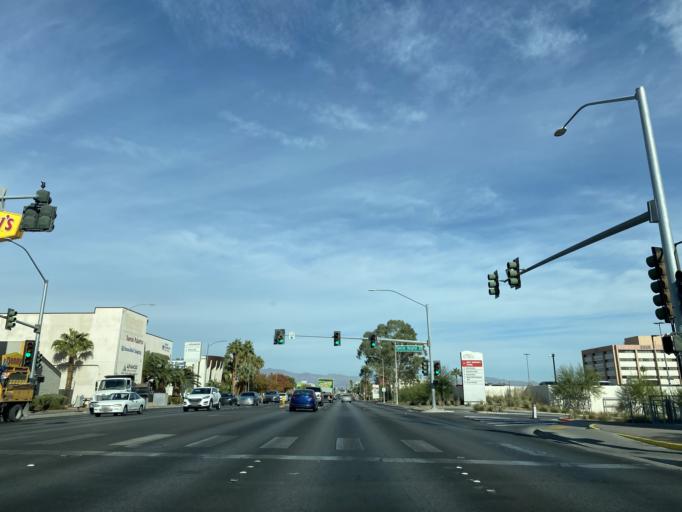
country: US
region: Nevada
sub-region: Clark County
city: Winchester
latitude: 36.1334
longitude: -115.1368
